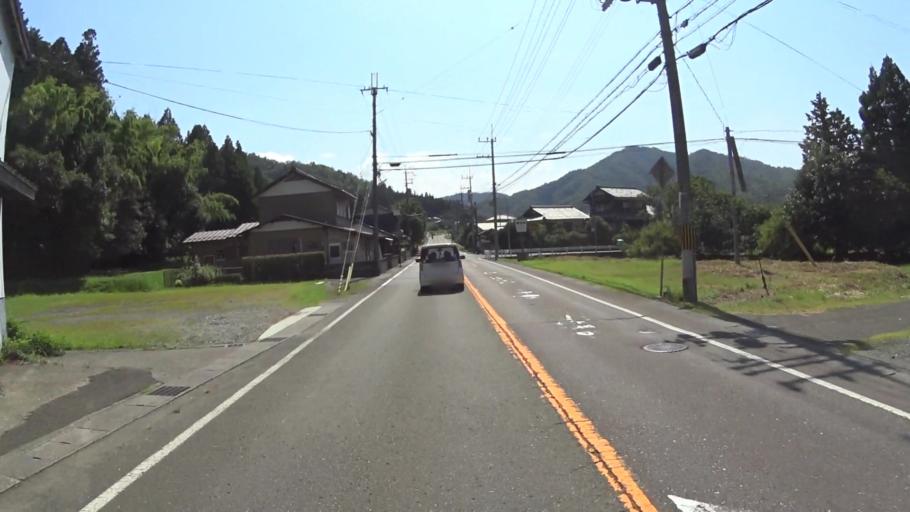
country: JP
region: Fukui
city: Obama
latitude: 35.4506
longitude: 135.7084
